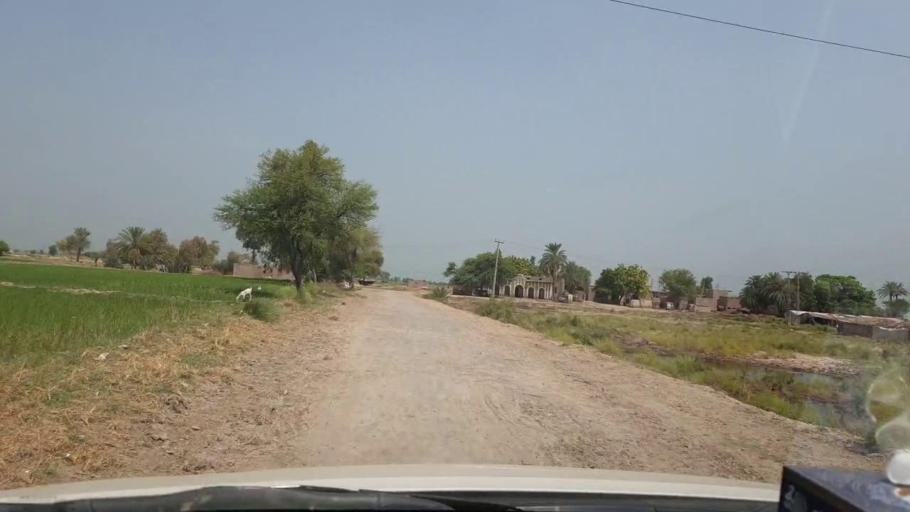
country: PK
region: Sindh
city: Shikarpur
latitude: 27.9920
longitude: 68.6963
